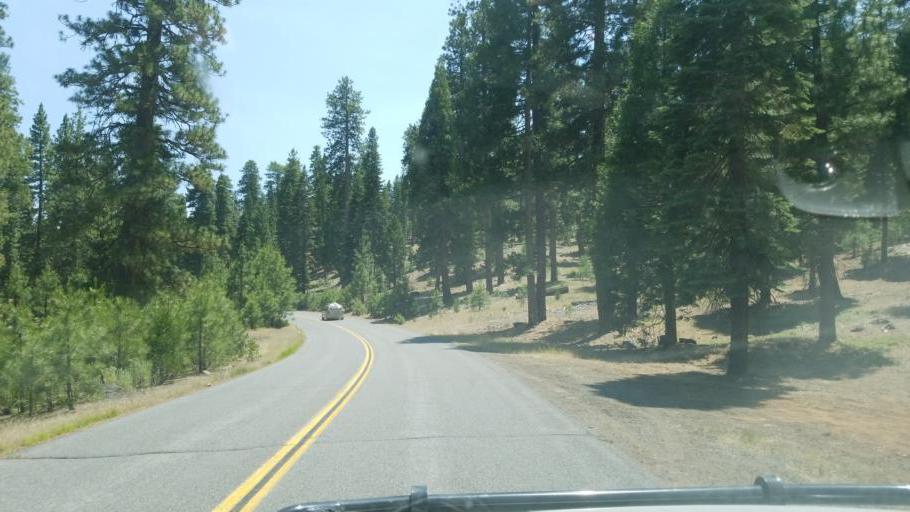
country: US
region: California
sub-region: Lassen County
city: Susanville
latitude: 40.5569
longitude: -120.8266
